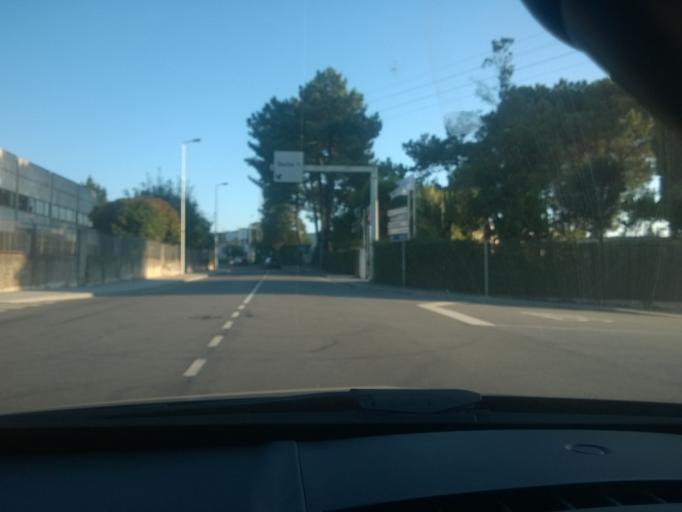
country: PT
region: Porto
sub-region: Maia
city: Gemunde
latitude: 41.2610
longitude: -8.6471
